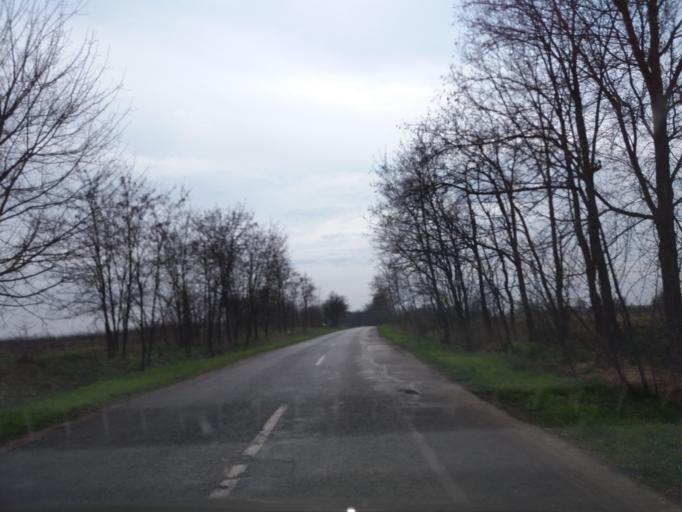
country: HU
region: Szabolcs-Szatmar-Bereg
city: Petnehaza
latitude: 48.0743
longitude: 22.0889
